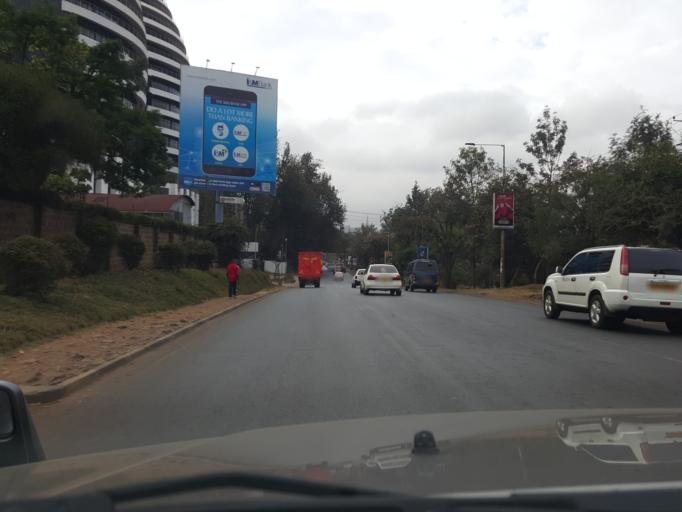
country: KE
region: Nairobi Area
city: Nairobi
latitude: -1.2693
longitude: 36.8064
